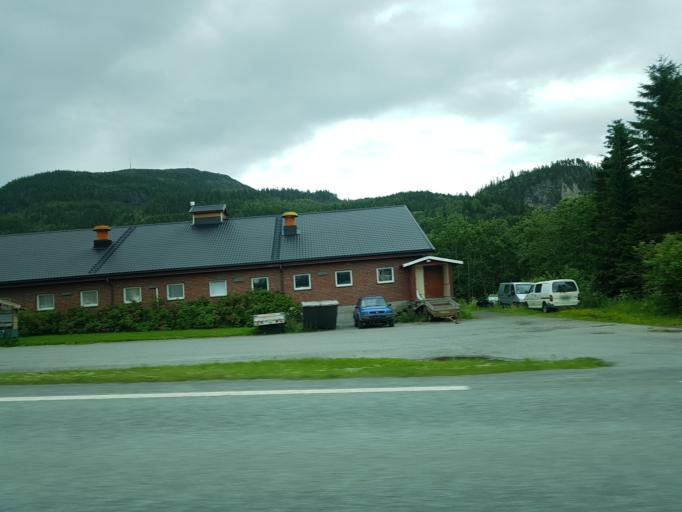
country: NO
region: Nord-Trondelag
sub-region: Stjordal
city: Stjordal
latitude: 63.5175
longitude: 10.8578
